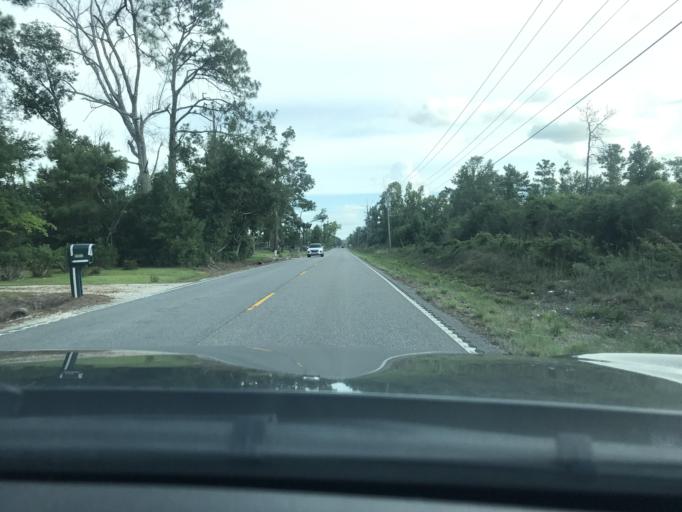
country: US
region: Louisiana
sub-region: Calcasieu Parish
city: Moss Bluff
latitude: 30.3195
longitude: -93.2583
